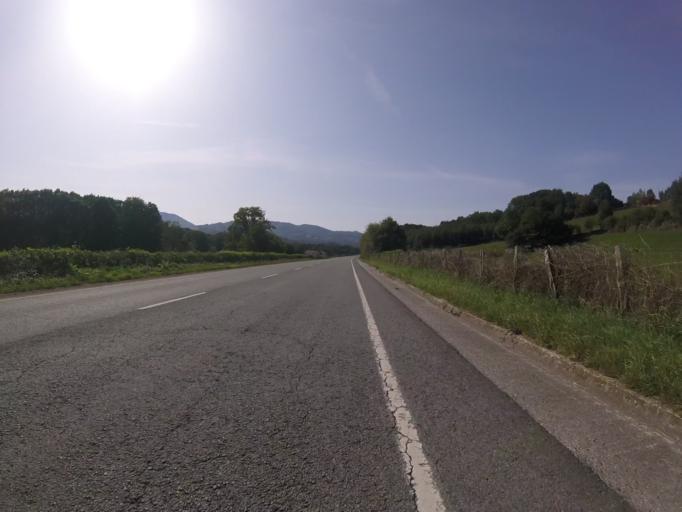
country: ES
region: Navarre
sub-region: Provincia de Navarra
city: Zugarramurdi
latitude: 43.1878
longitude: -1.4864
